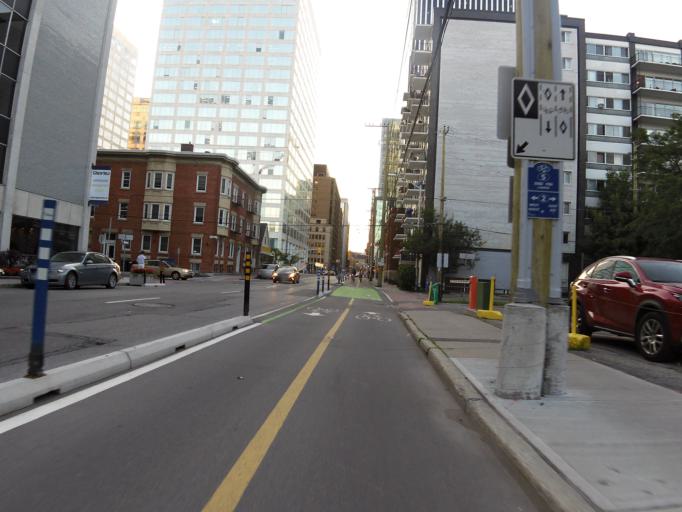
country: CA
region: Ontario
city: Ottawa
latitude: 45.4179
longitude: -75.6957
